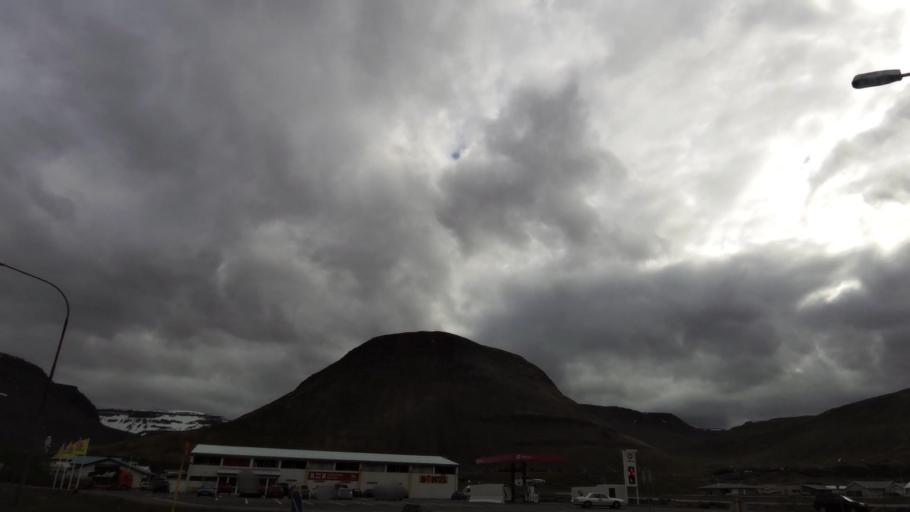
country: IS
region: Westfjords
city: Isafjoerdur
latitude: 66.0611
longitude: -23.1749
